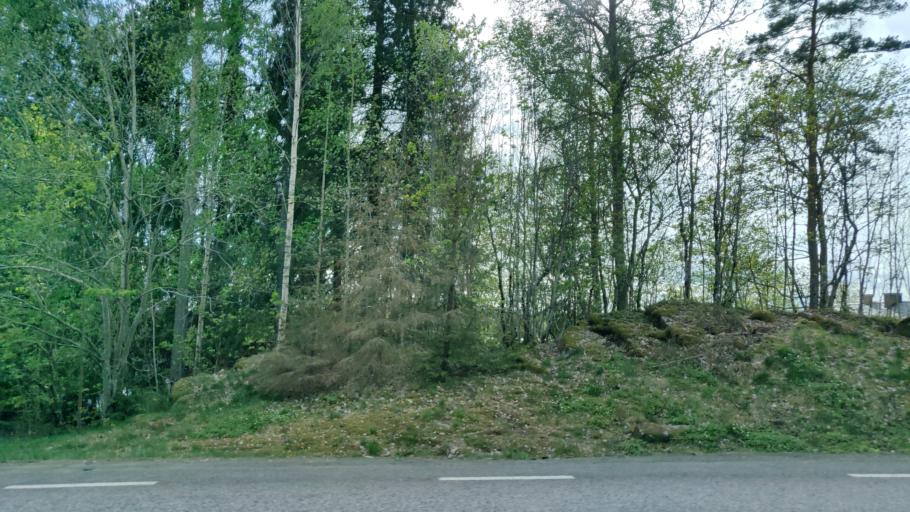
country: SE
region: Vaermland
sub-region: Forshaga Kommun
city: Deje
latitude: 59.5900
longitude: 13.4572
